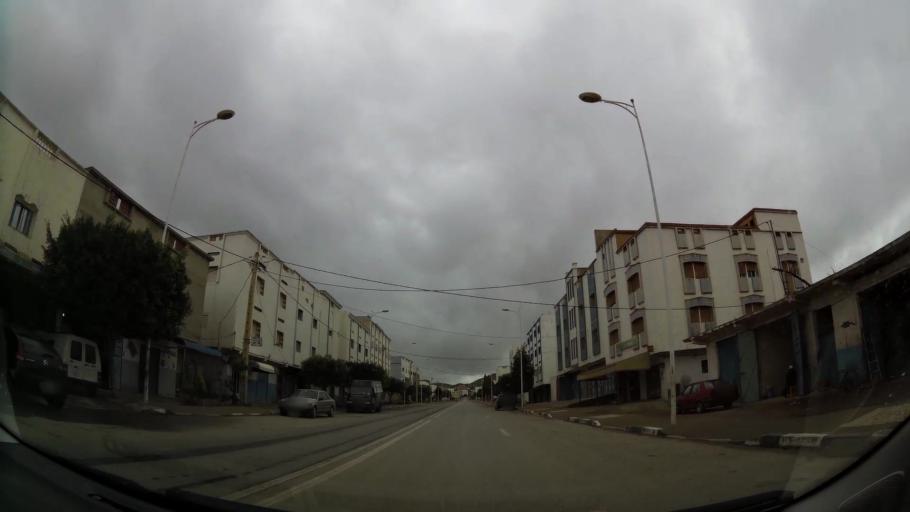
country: MA
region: Oriental
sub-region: Nador
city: Midar
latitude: 35.0515
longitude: -3.4608
